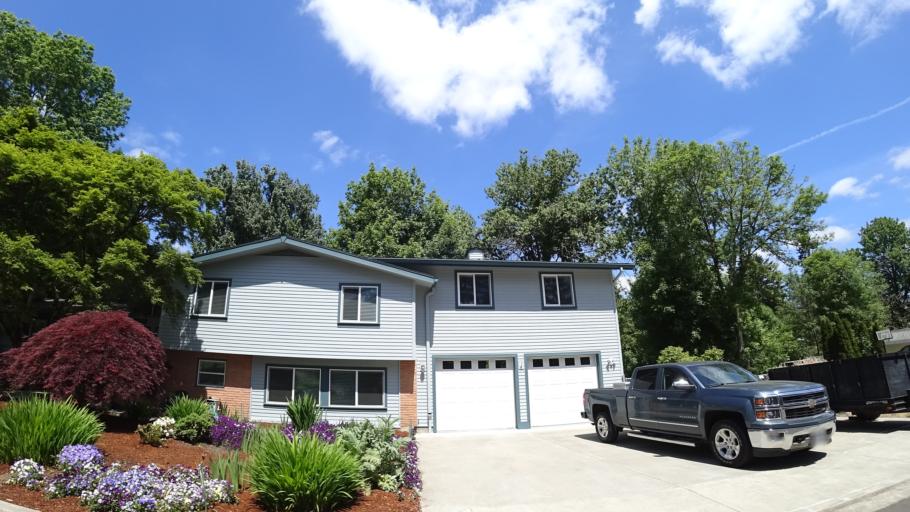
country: US
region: Oregon
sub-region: Washington County
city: Tigard
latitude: 45.4340
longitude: -122.7961
